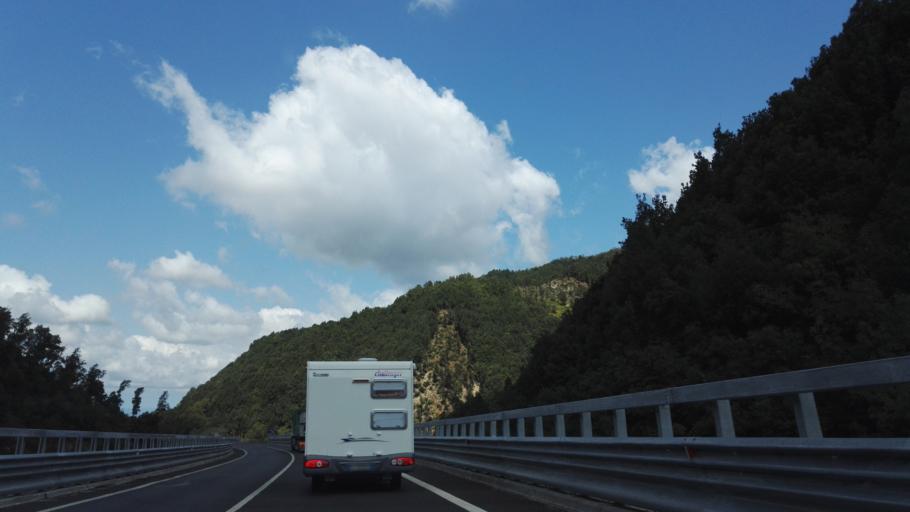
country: IT
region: Calabria
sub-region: Provincia di Reggio Calabria
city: Giffone
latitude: 38.4125
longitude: 16.1391
